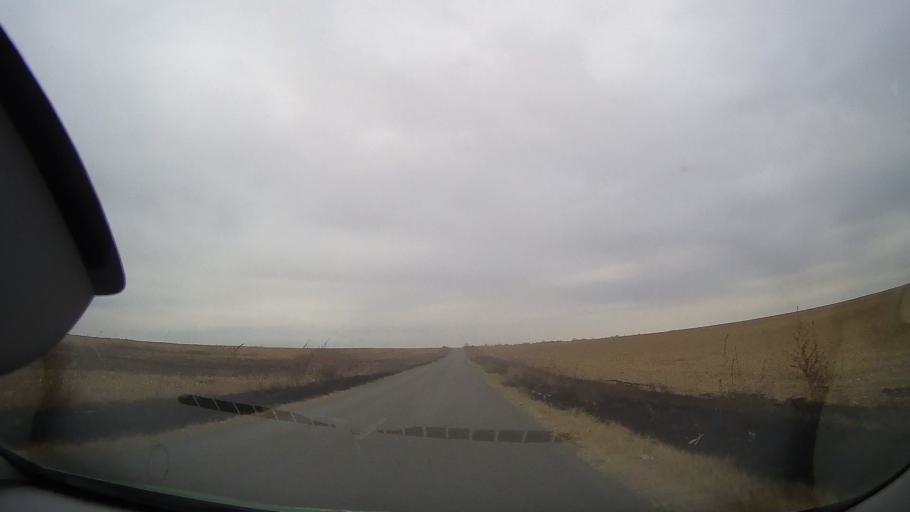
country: RO
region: Buzau
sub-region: Comuna Rusetu
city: Rusetu
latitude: 44.9672
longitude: 27.1944
